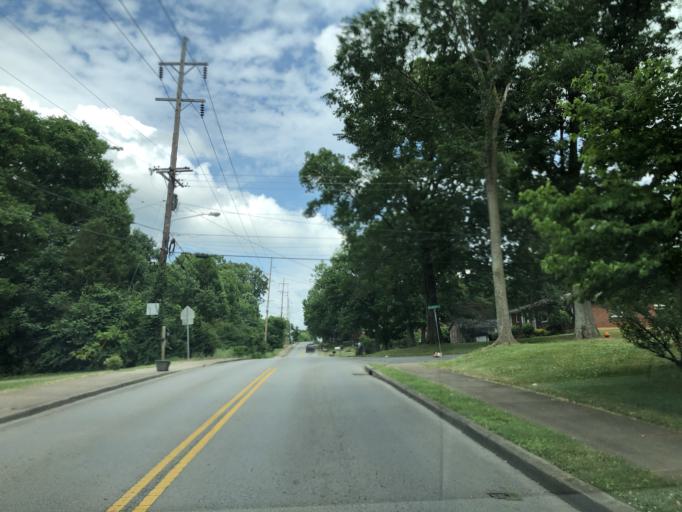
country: US
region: Tennessee
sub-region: Davidson County
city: Goodlettsville
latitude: 36.2730
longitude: -86.7015
